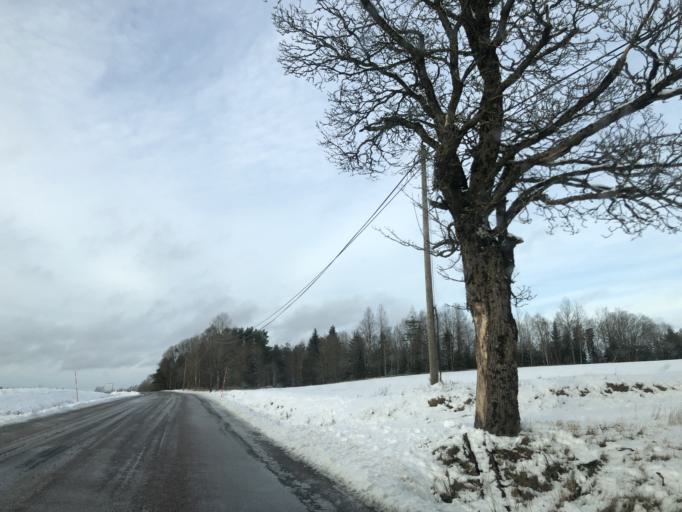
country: SE
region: Vaestra Goetaland
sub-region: Ulricehamns Kommun
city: Ulricehamn
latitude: 57.8123
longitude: 13.5363
